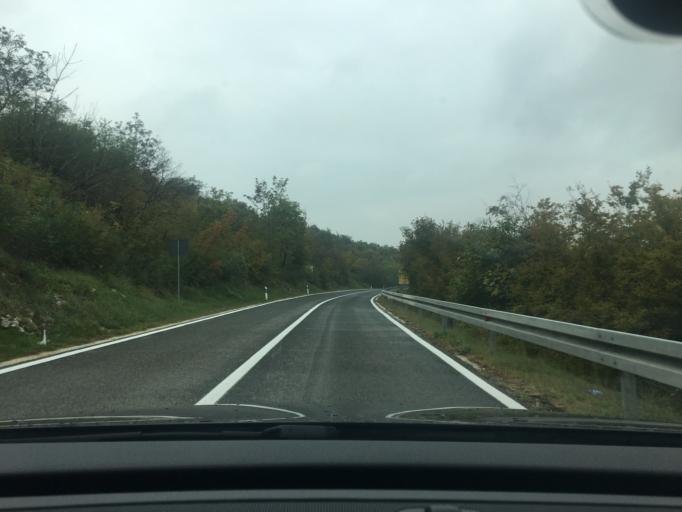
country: HR
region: Istarska
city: Buje
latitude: 45.4516
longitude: 13.6473
